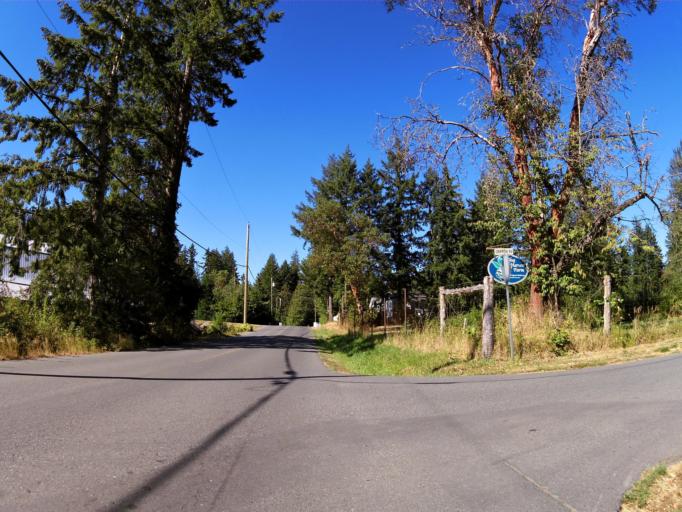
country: CA
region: British Columbia
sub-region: Cowichan Valley Regional District
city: Ladysmith
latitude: 49.0410
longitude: -123.8508
